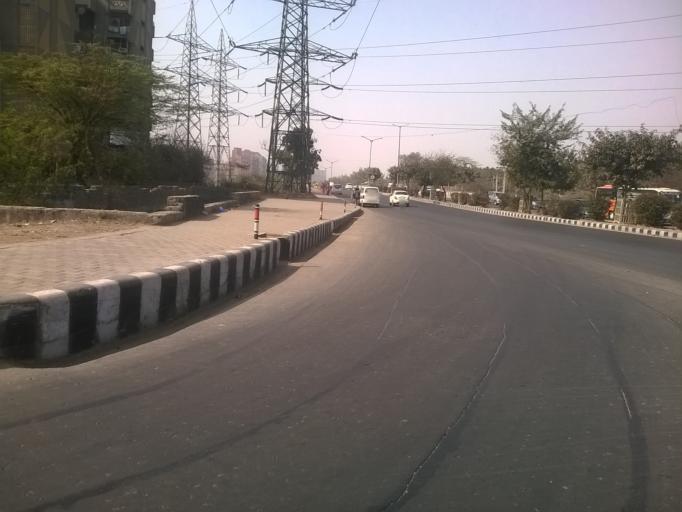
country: IN
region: NCT
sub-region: West Delhi
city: Nangloi Jat
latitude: 28.5984
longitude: 77.0632
